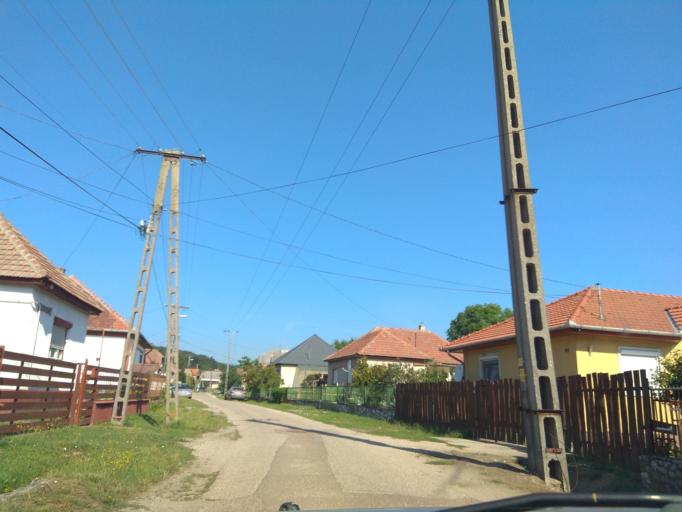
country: HU
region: Borsod-Abauj-Zemplen
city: Harsany
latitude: 47.9835
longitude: 20.7823
